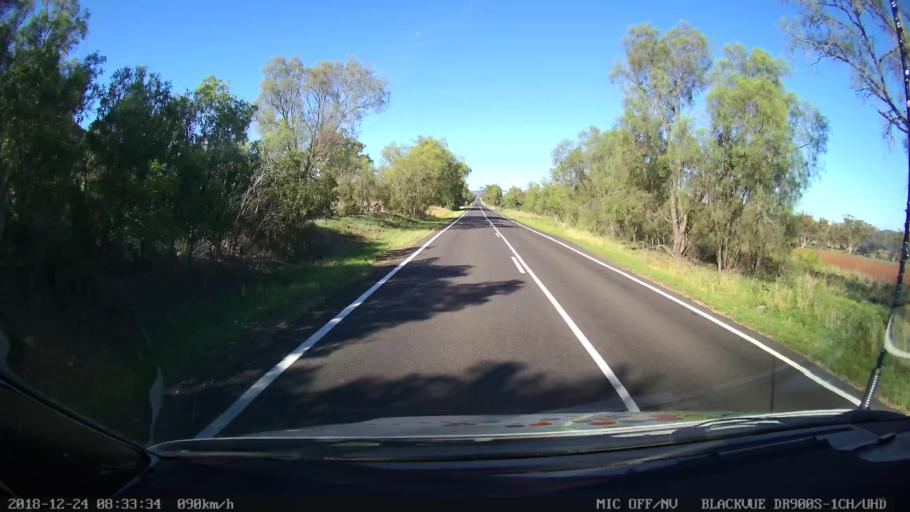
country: AU
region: New South Wales
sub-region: Liverpool Plains
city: Quirindi
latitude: -31.2871
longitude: 150.6828
